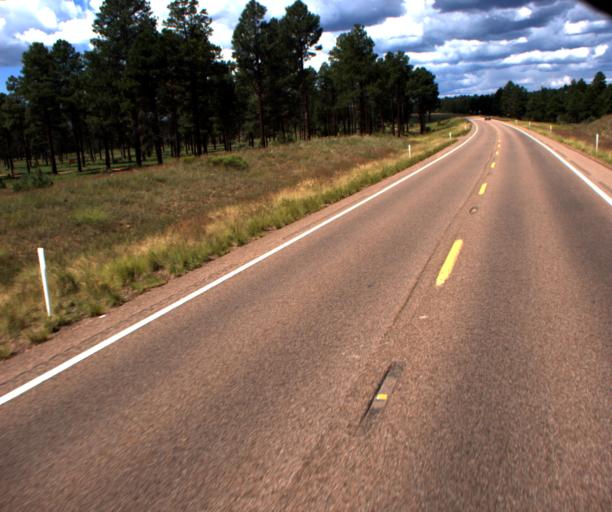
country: US
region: Arizona
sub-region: Navajo County
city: Heber-Overgaard
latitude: 34.3930
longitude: -110.5140
